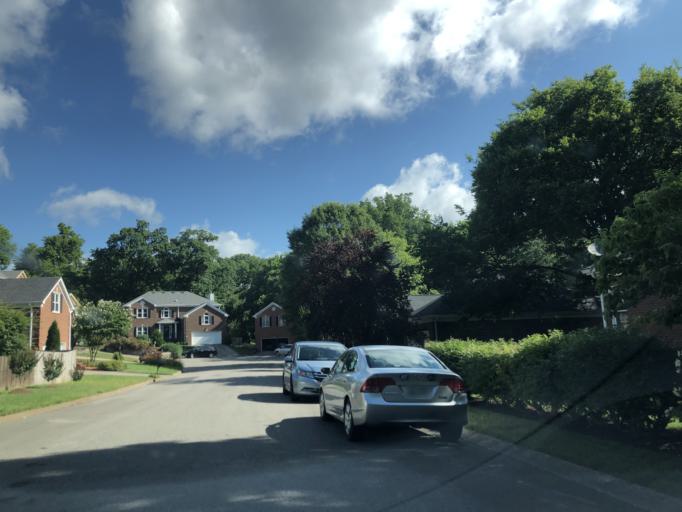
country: US
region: Tennessee
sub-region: Cheatham County
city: Pegram
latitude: 36.0612
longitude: -86.9559
